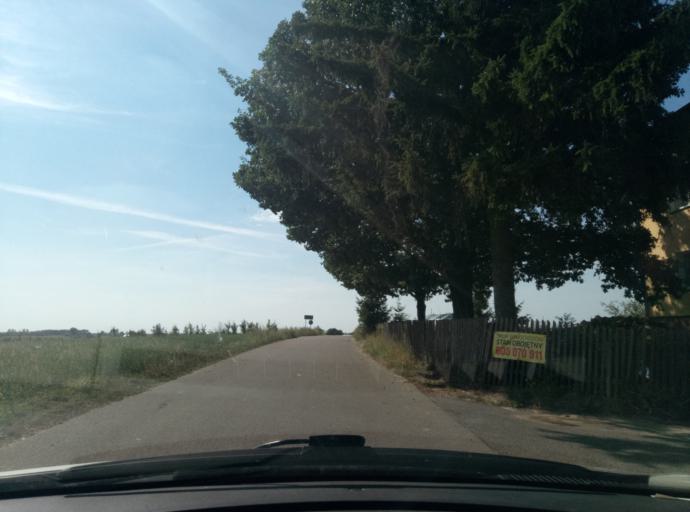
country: PL
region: Kujawsko-Pomorskie
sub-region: Powiat brodnicki
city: Jablonowo Pomorskie
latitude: 53.4139
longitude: 19.2540
